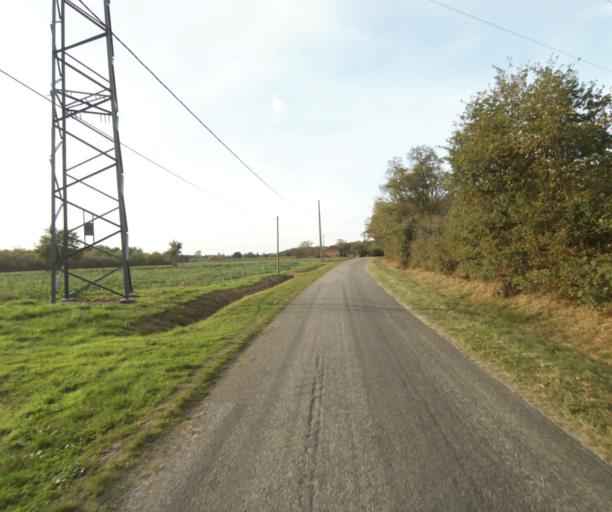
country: FR
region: Midi-Pyrenees
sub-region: Departement du Tarn-et-Garonne
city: Campsas
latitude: 43.8752
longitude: 1.3263
